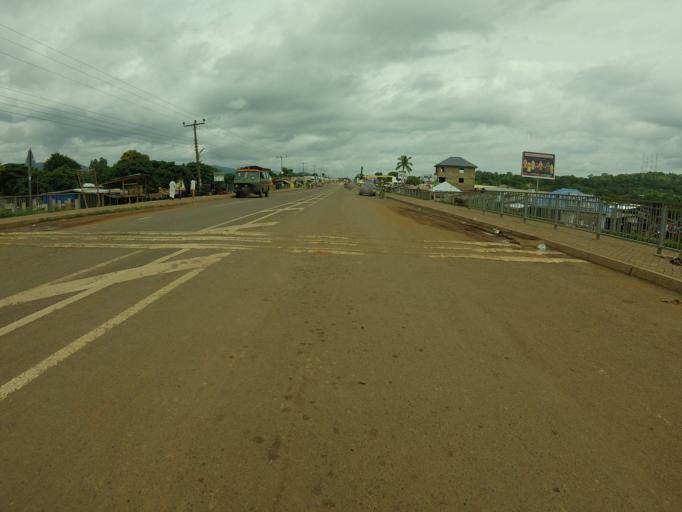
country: TG
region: Centrale
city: Sotouboua
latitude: 8.2665
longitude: 0.5198
